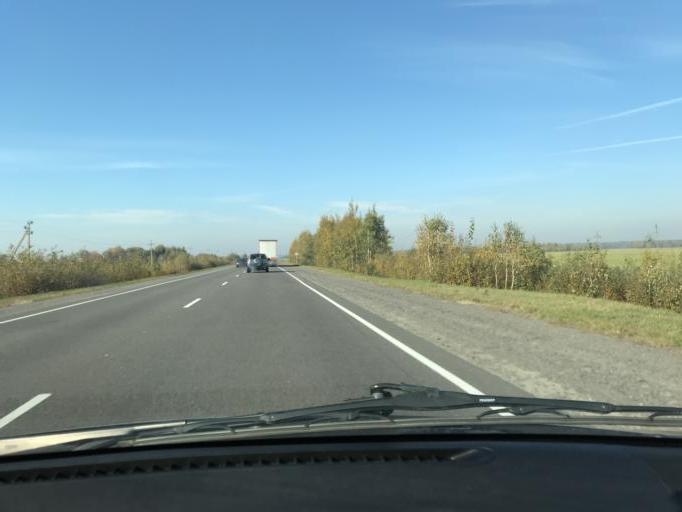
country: BY
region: Brest
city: Horad Luninyets
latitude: 52.3128
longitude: 26.6571
